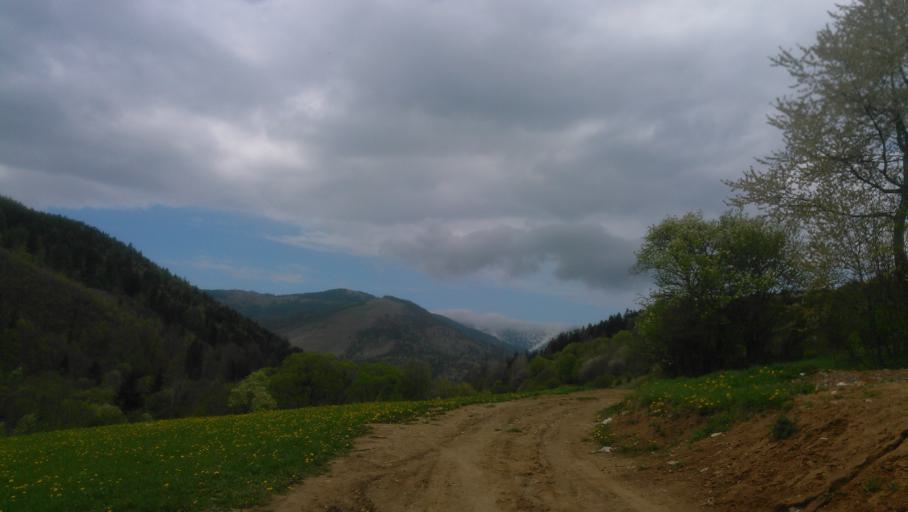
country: SK
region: Banskobystricky
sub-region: Okres Banska Bystrica
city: Brezno
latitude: 48.8488
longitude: 19.6085
